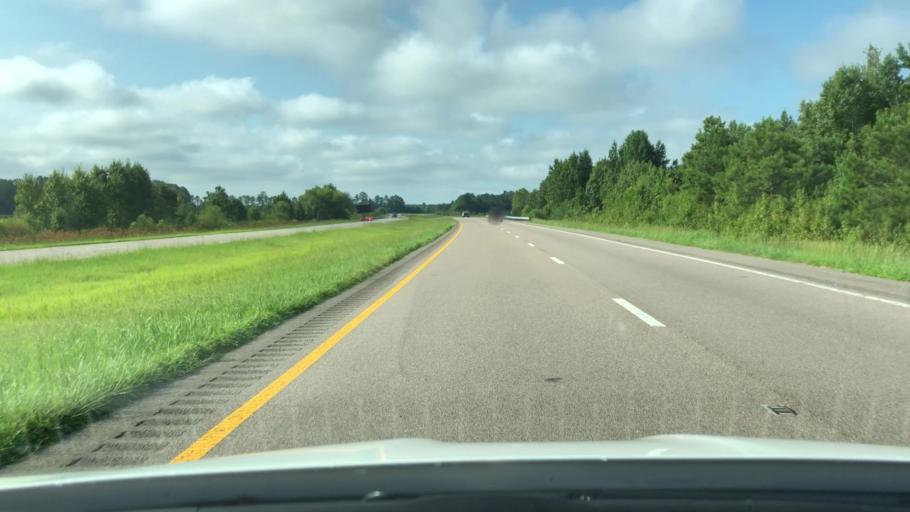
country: US
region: Virginia
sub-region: City of Portsmouth
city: Portsmouth Heights
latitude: 36.6865
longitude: -76.3475
